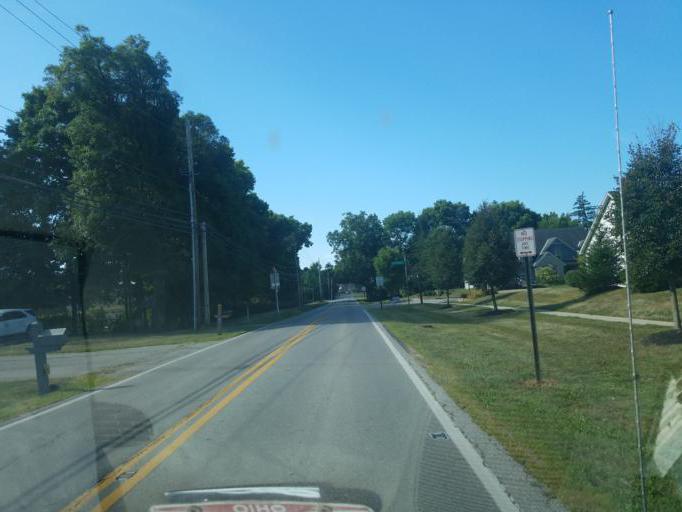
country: US
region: Ohio
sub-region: Franklin County
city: Worthington
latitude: 40.1104
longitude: -83.0426
